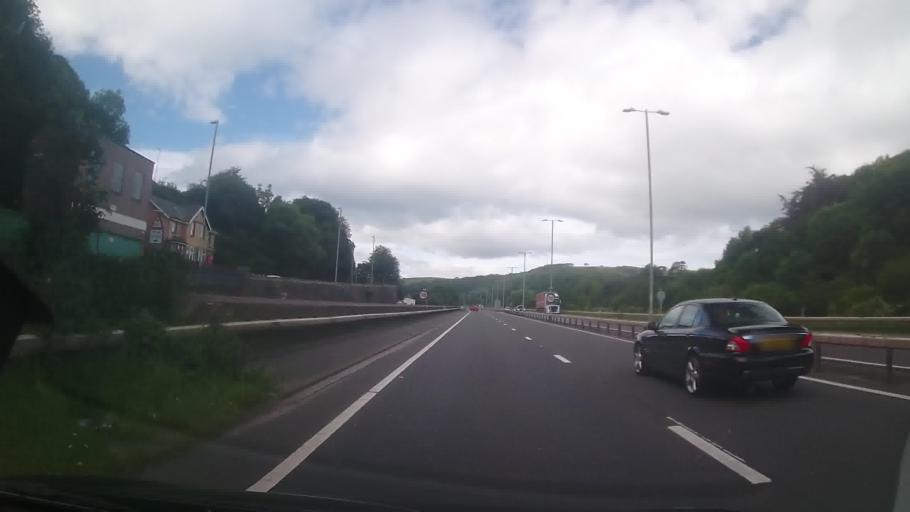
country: GB
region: Wales
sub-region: Conwy
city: Mochdre
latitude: 53.2988
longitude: -3.7533
